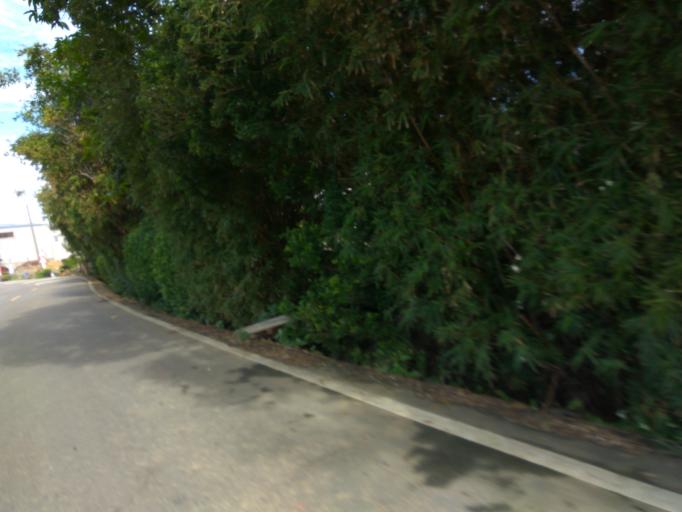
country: TW
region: Taiwan
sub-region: Hsinchu
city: Zhubei
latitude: 24.9937
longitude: 121.0954
